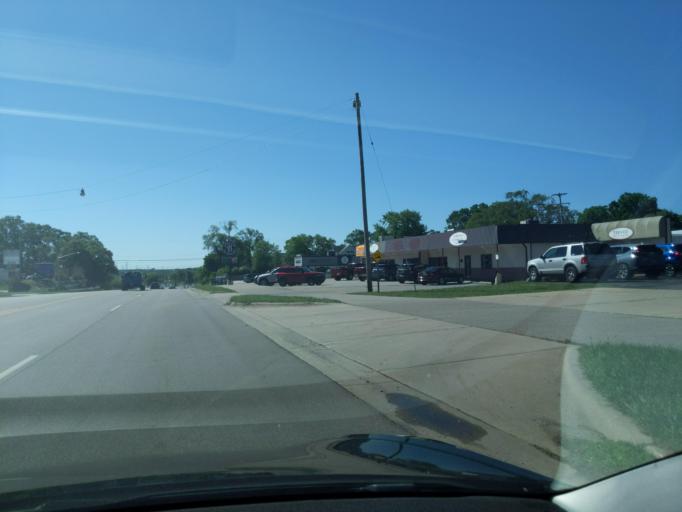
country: US
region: Michigan
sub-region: Muskegon County
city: North Muskegon
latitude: 43.2680
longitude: -86.2526
